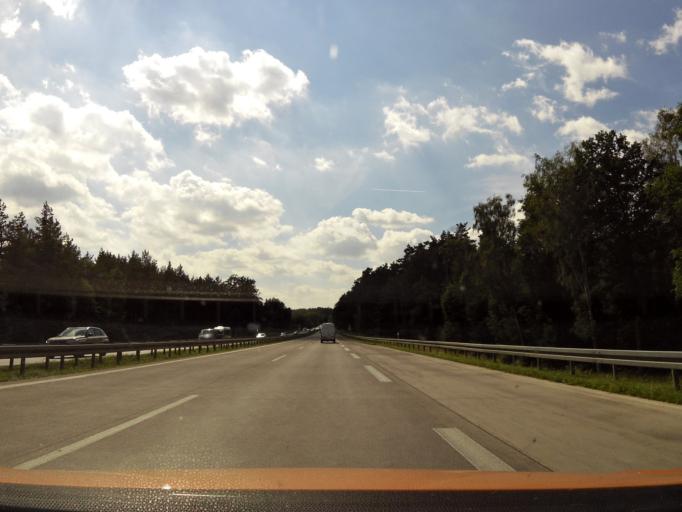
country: DE
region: Brandenburg
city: Althuttendorf
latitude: 52.9370
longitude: 13.7911
